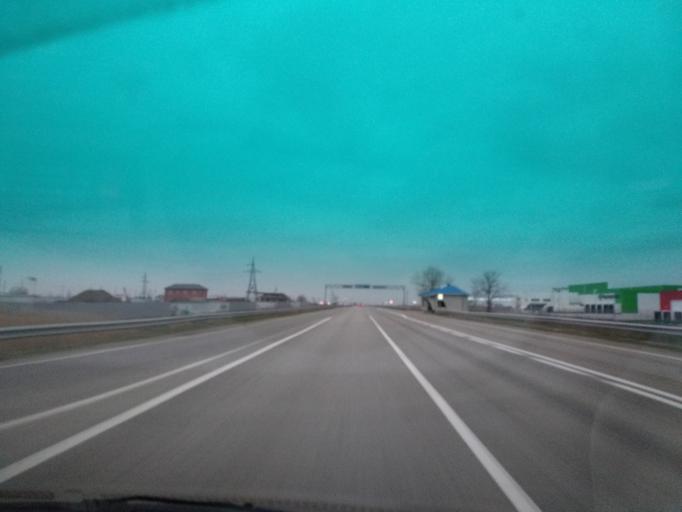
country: RU
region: Adygeya
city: Adygeysk
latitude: 44.8748
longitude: 39.1821
